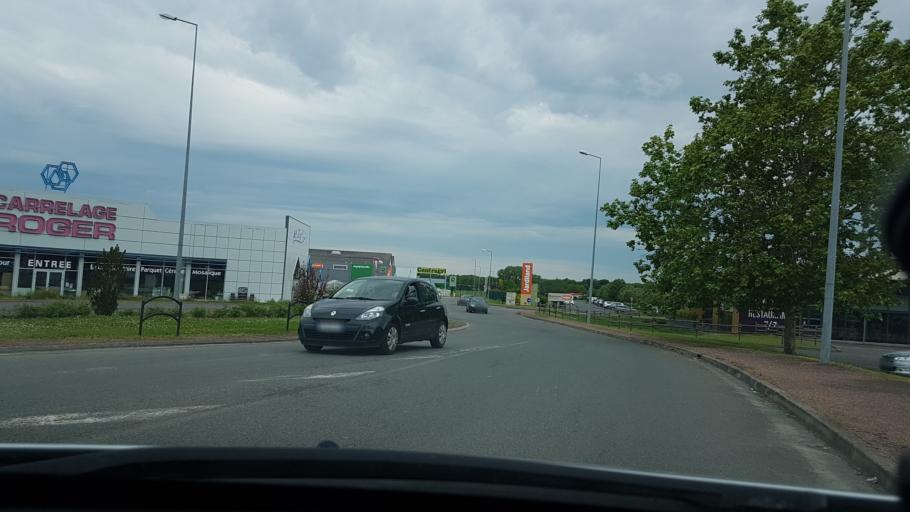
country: FR
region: Centre
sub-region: Departement du Cher
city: Saint-Germain-du-Puy
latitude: 47.0970
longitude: 2.4552
